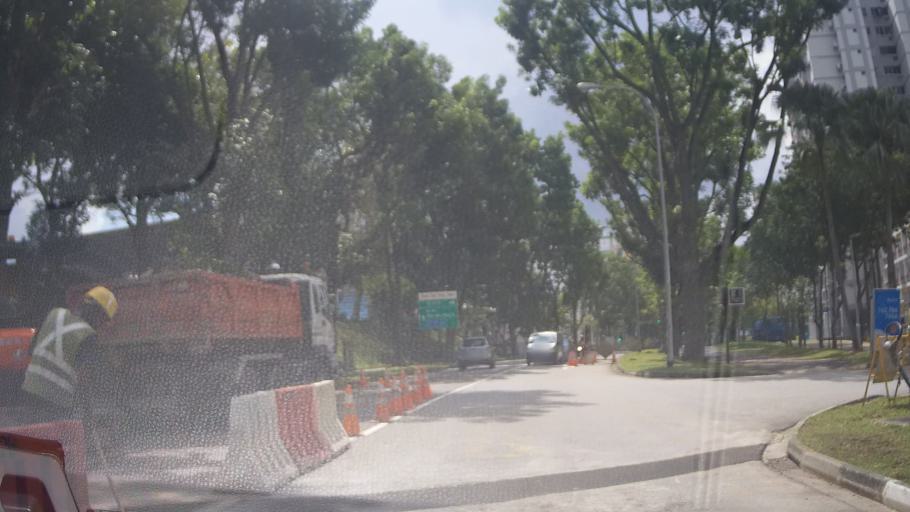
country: MY
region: Johor
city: Johor Bahru
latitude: 1.3924
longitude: 103.7498
